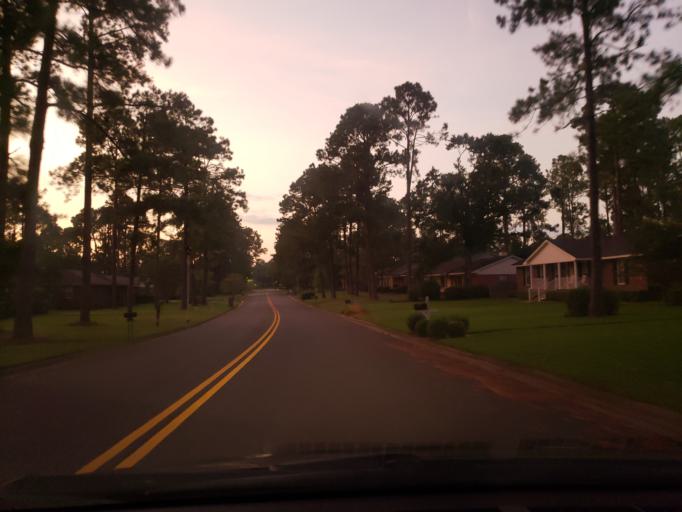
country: US
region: Georgia
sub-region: Dougherty County
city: Albany
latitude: 31.5928
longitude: -84.2039
